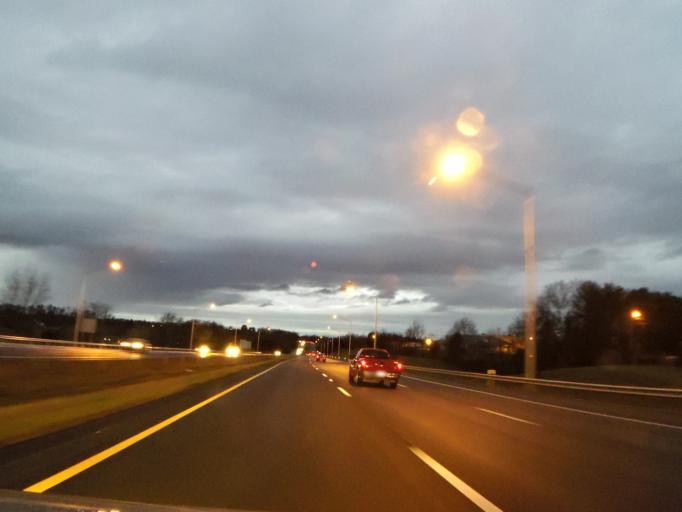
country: US
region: Tennessee
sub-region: Washington County
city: Gray
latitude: 36.4087
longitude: -82.4807
